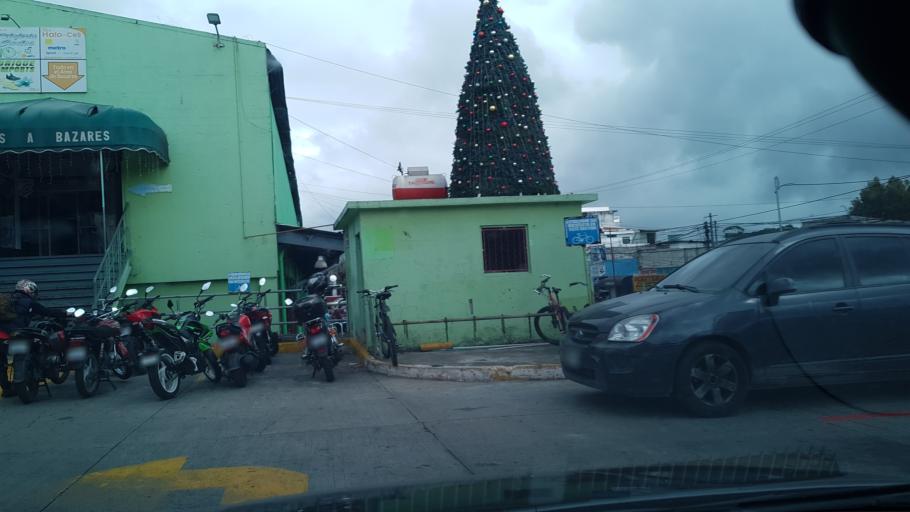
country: GT
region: Guatemala
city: Mixco
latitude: 14.6449
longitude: -90.5746
